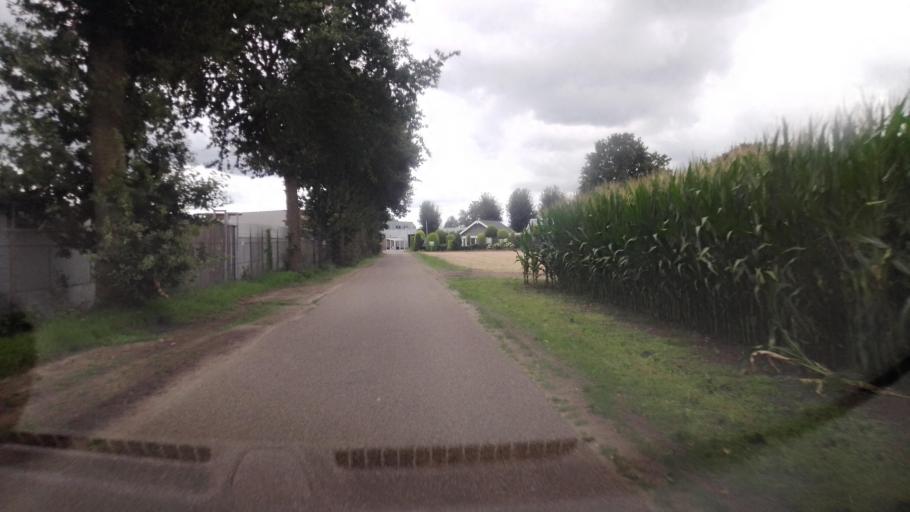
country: NL
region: Limburg
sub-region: Gemeente Peel en Maas
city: Maasbree
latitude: 51.3634
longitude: 6.0591
